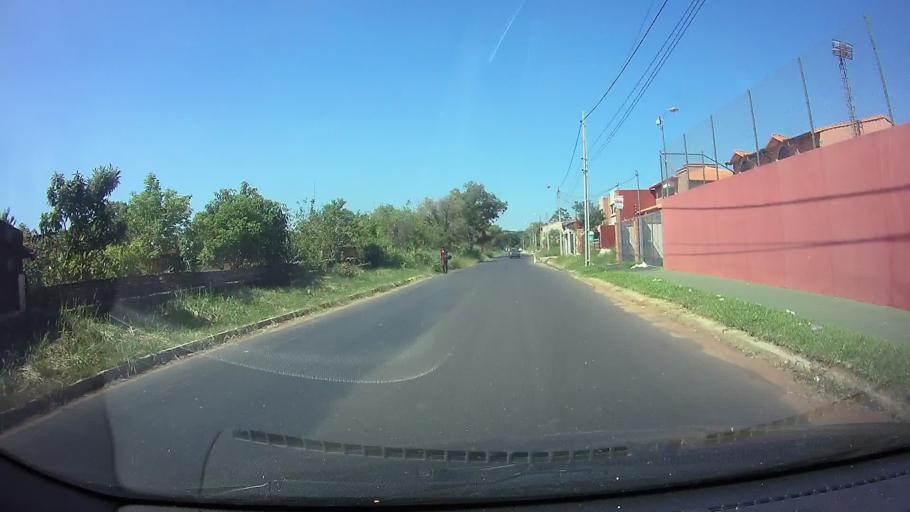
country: PY
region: Central
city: Fernando de la Mora
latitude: -25.2846
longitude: -57.5447
